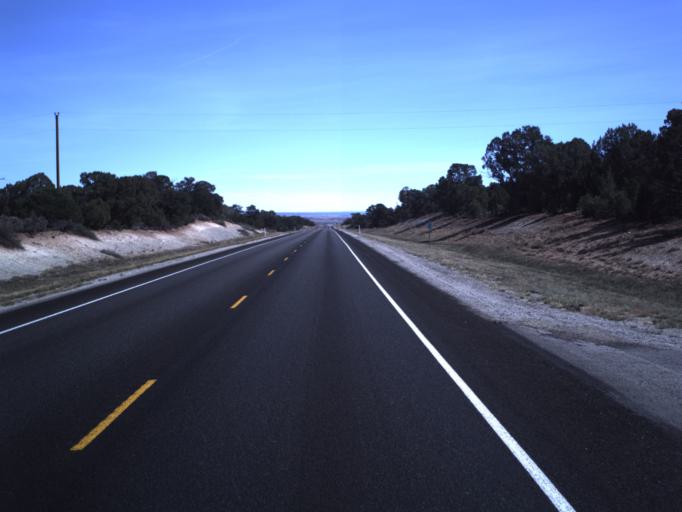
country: US
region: Colorado
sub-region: Dolores County
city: Dove Creek
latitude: 37.8267
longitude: -109.0775
